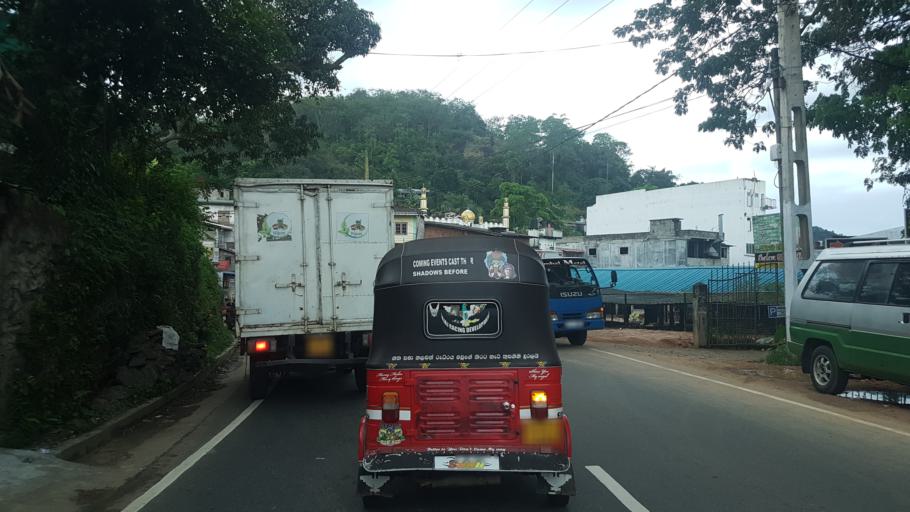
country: LK
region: Western
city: Hanwella Ihala
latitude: 7.0302
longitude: 80.2954
